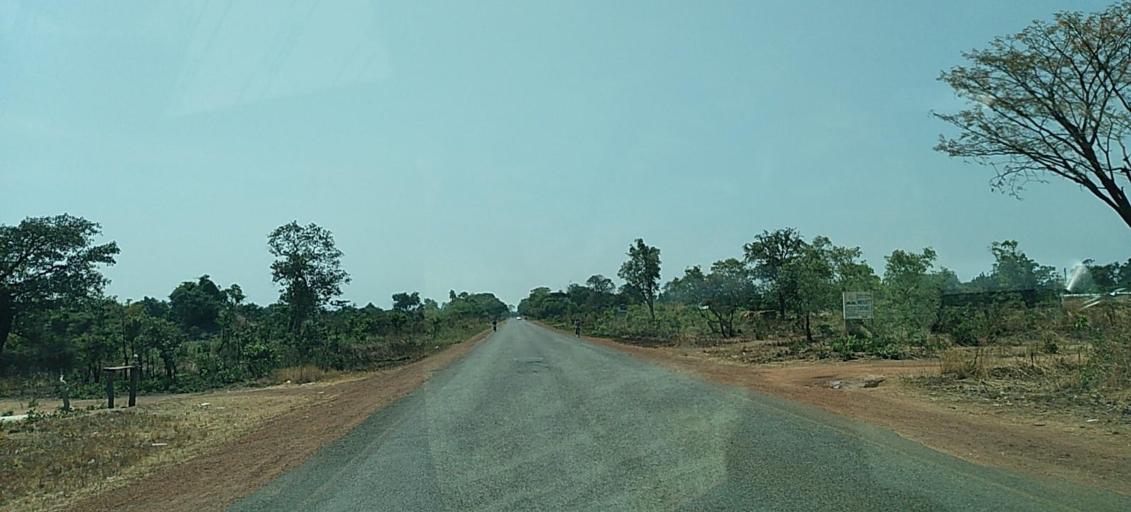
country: ZM
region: North-Western
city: Solwezi
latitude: -12.3189
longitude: 25.8672
